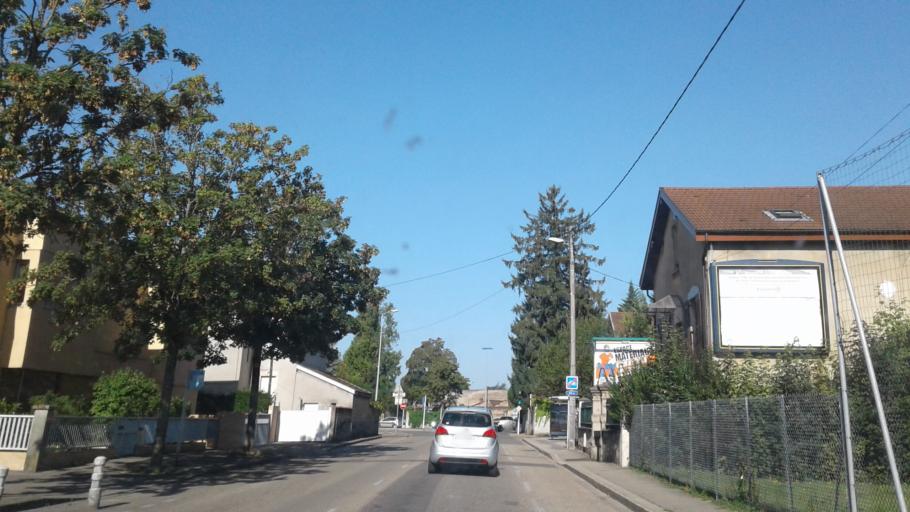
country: FR
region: Rhone-Alpes
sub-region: Departement de l'Ain
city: Bourg-en-Bresse
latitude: 46.1958
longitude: 5.2205
